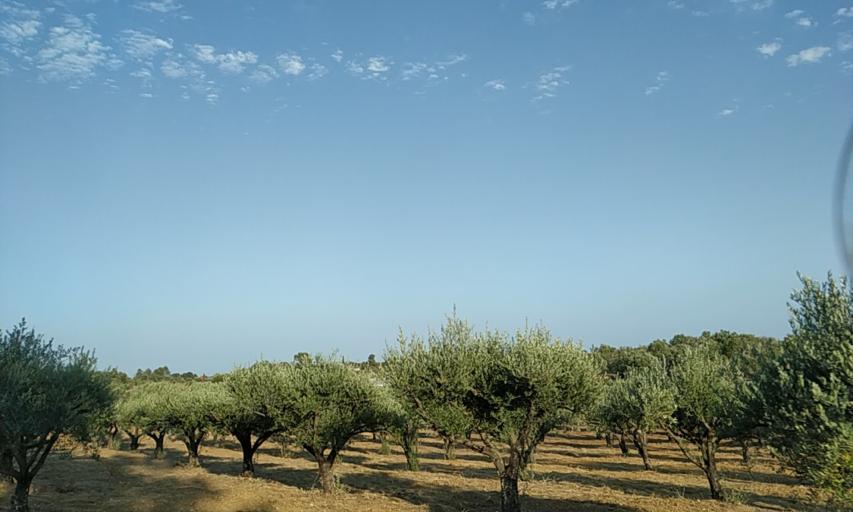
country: PT
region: Santarem
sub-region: Alcanena
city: Alcanena
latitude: 39.4320
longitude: -8.6307
